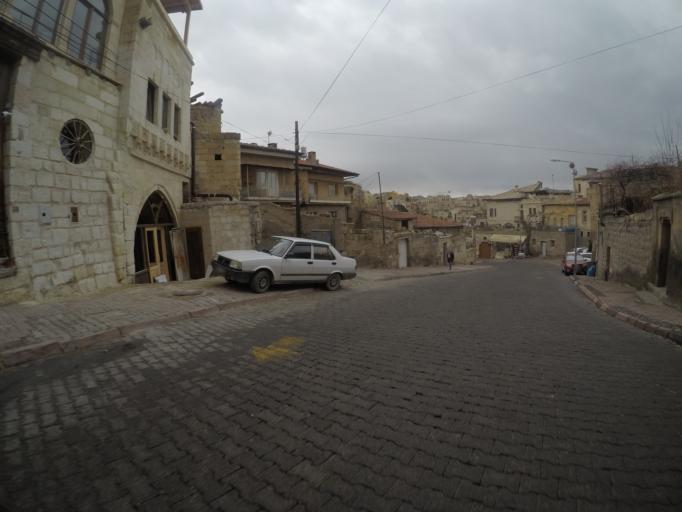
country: TR
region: Nevsehir
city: Urgub
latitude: 38.6327
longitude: 34.9082
